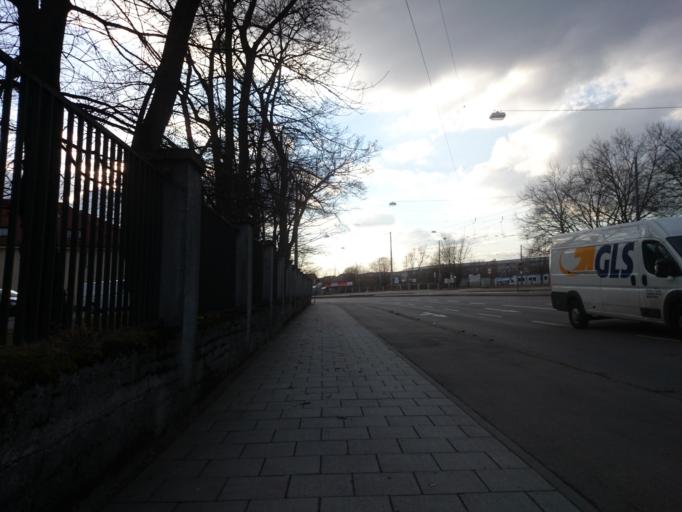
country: DE
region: Bavaria
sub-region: Upper Bavaria
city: Munich
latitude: 48.1613
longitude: 11.5522
